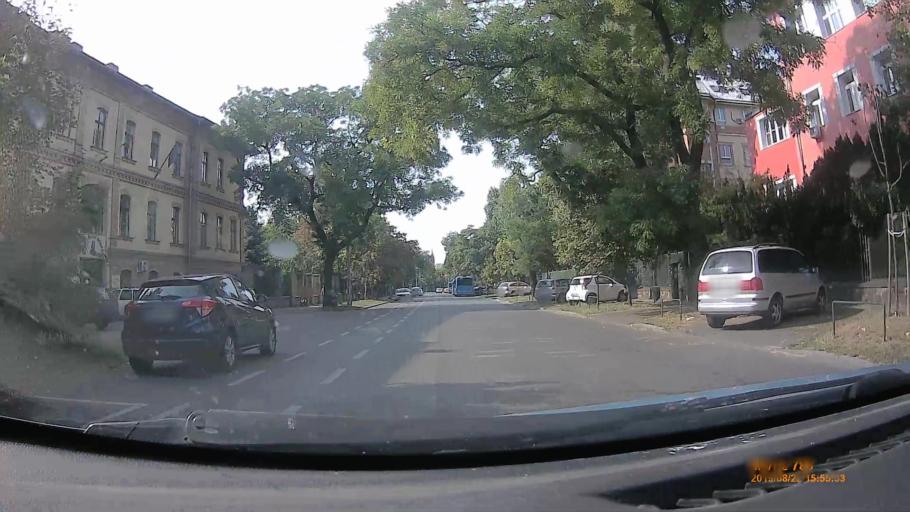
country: HU
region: Budapest
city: Budapest VIII. keruelet
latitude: 47.4755
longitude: 19.0927
